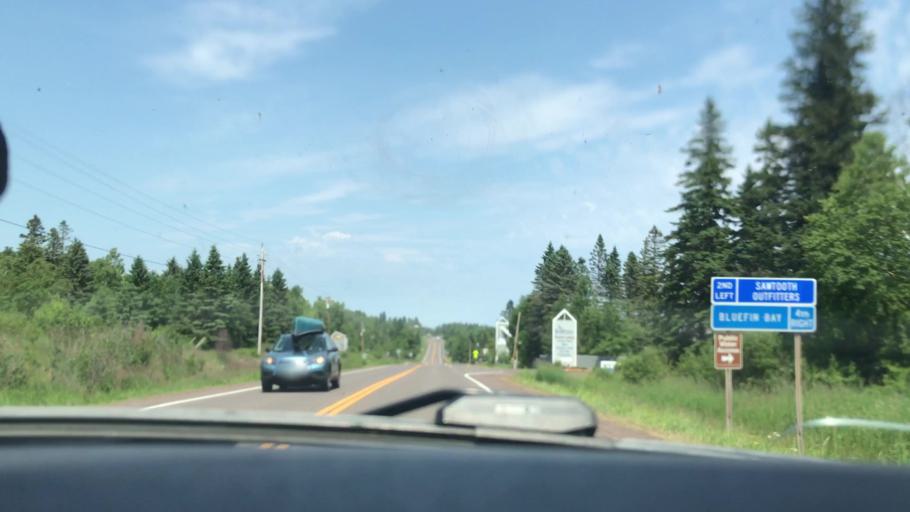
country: US
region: Minnesota
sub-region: Lake County
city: Silver Bay
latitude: 47.5728
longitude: -90.8389
